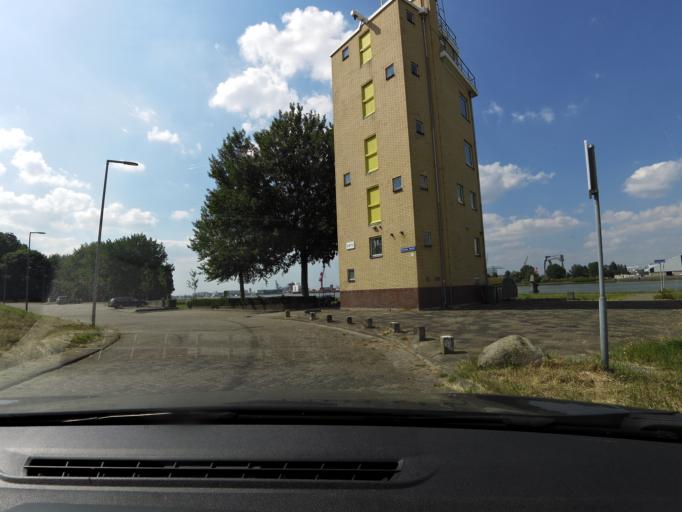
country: NL
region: South Holland
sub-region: Gemeente Schiedam
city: Schiedam
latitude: 51.8941
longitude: 4.3893
